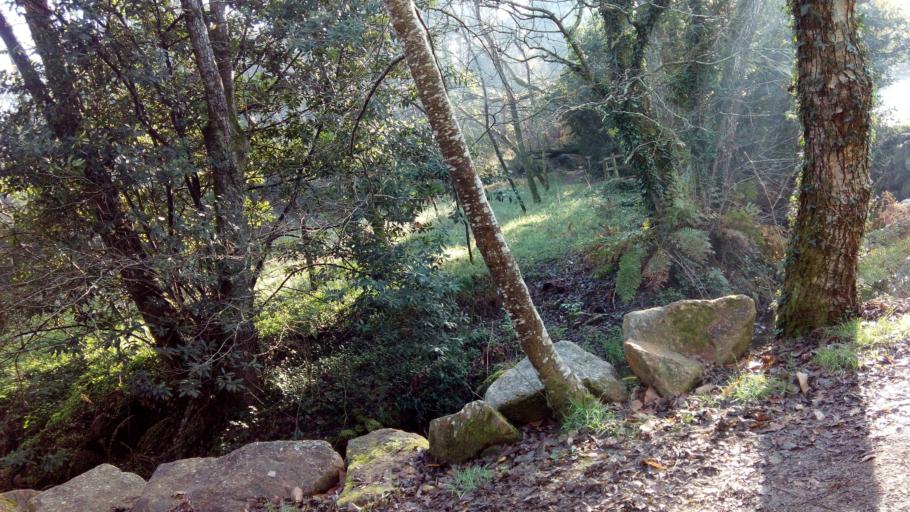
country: ES
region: Galicia
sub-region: Provincia de Pontevedra
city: Meis
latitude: 42.4897
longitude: -8.7527
